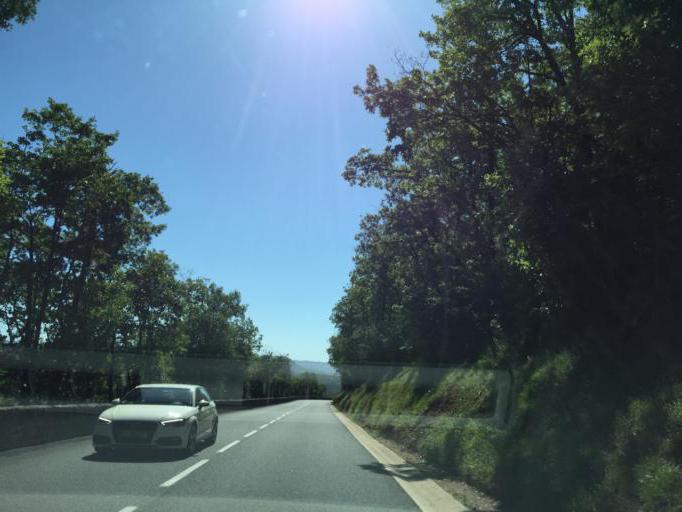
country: FR
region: Midi-Pyrenees
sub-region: Departement de l'Aveyron
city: Saint-Georges-de-Luzencon
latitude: 44.0753
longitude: 2.8989
